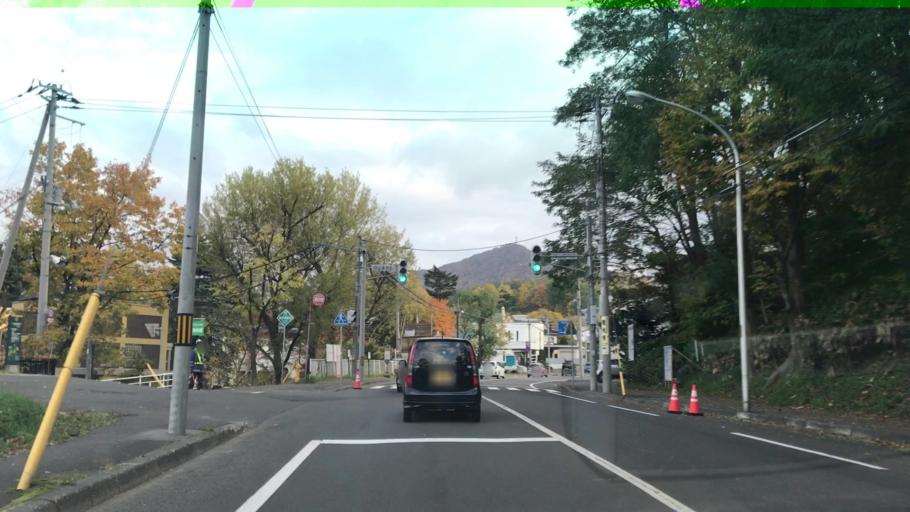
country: JP
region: Hokkaido
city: Sapporo
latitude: 43.0458
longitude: 141.3051
